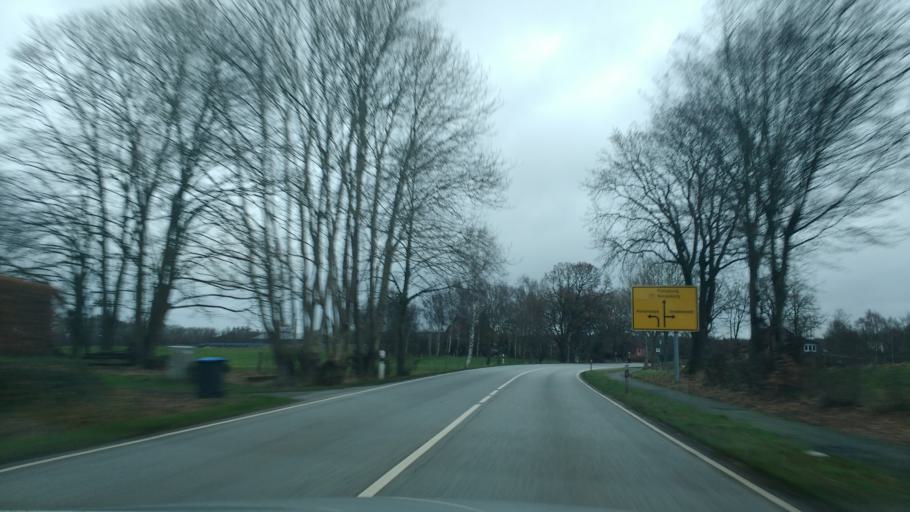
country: DE
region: Schleswig-Holstein
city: Schlotfeld
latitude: 53.9714
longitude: 9.5713
